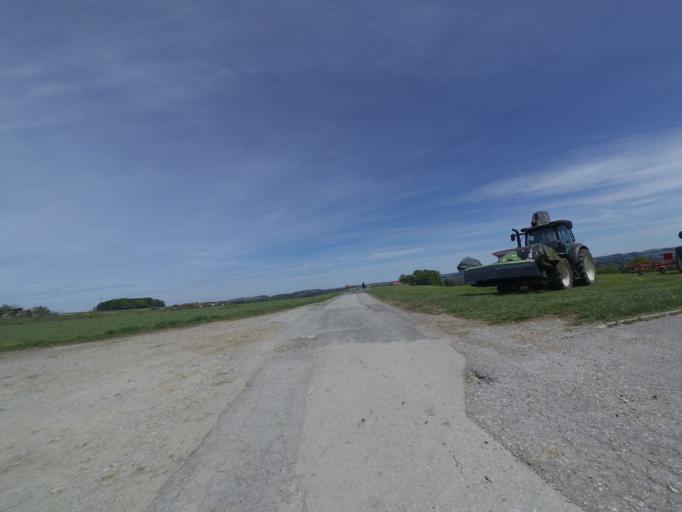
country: AT
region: Salzburg
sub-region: Politischer Bezirk Salzburg-Umgebung
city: Berndorf bei Salzburg
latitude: 47.9867
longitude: 13.0743
